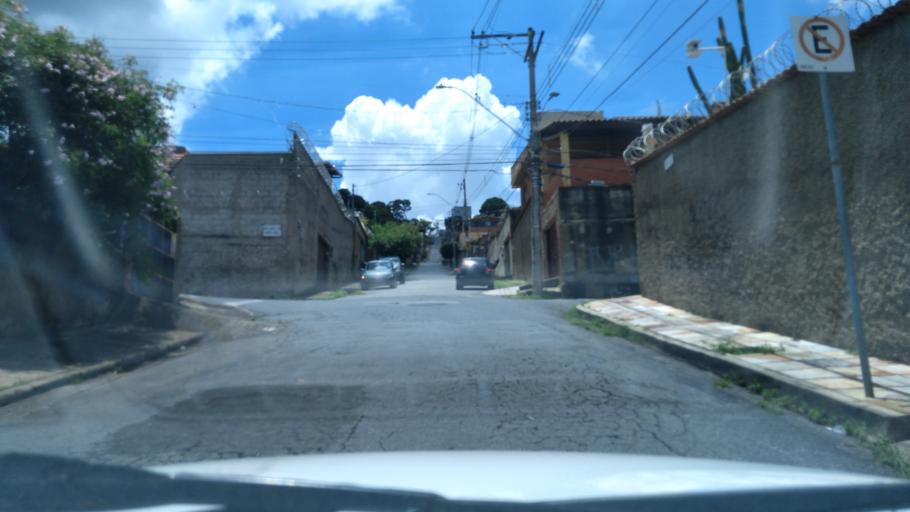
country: BR
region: Minas Gerais
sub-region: Belo Horizonte
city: Belo Horizonte
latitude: -19.9223
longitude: -43.9017
